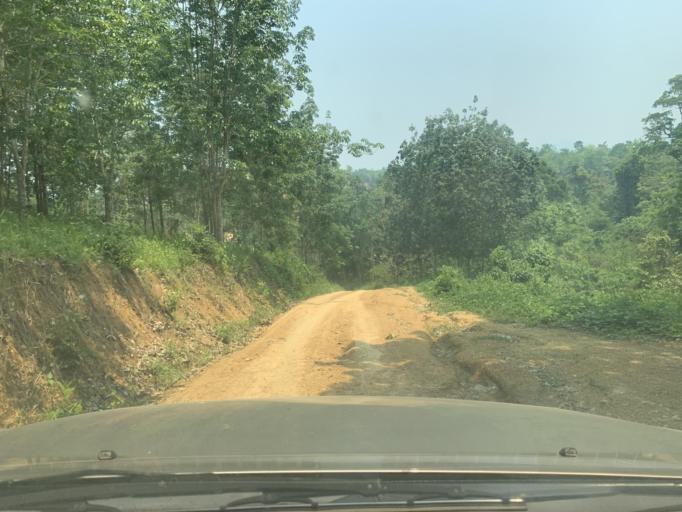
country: LA
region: Louangphabang
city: Xiang Ngeun
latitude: 19.8322
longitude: 102.2239
